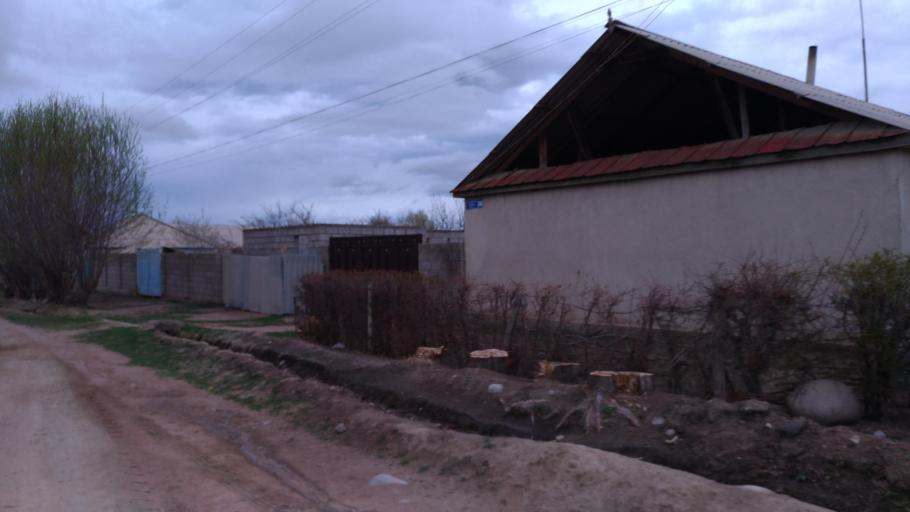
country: KG
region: Ysyk-Koel
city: Bokombayevskoye
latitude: 42.1110
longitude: 76.9830
